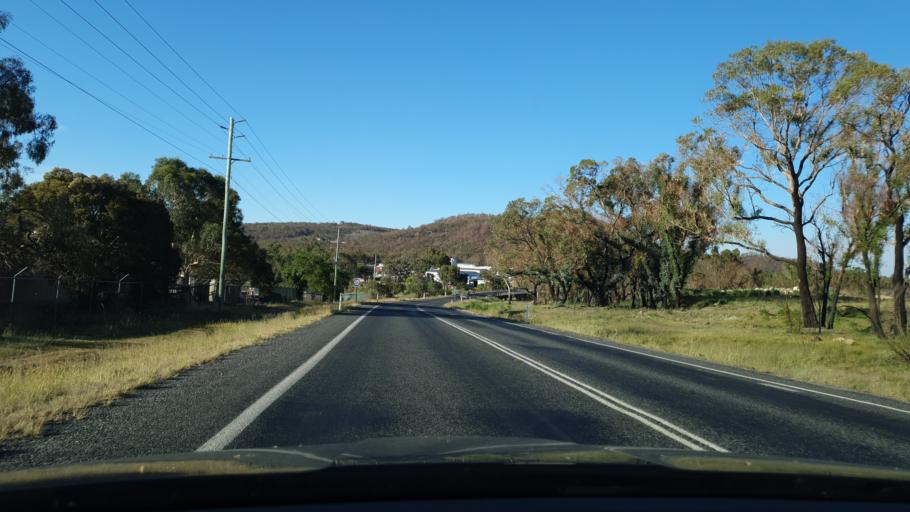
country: AU
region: Queensland
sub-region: Southern Downs
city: Stanthorpe
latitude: -28.6561
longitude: 151.9173
